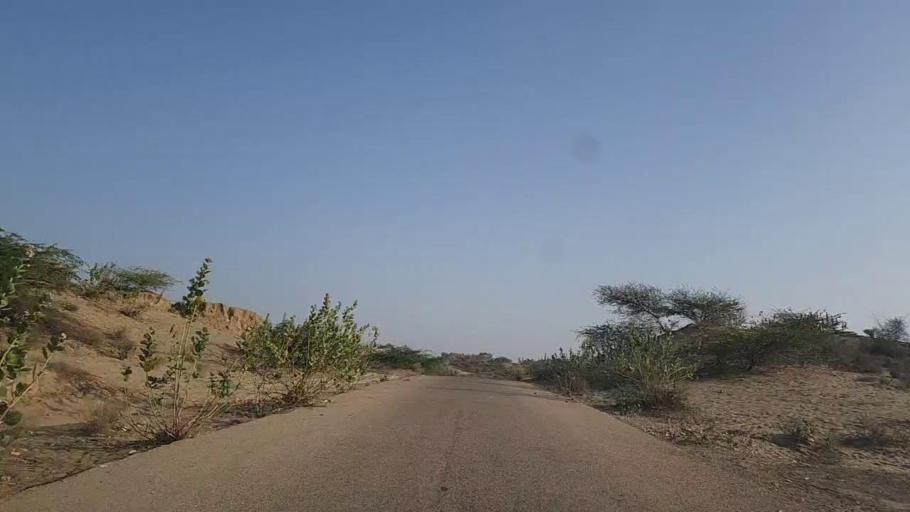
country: PK
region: Sindh
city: Diplo
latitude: 24.6048
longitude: 69.3795
